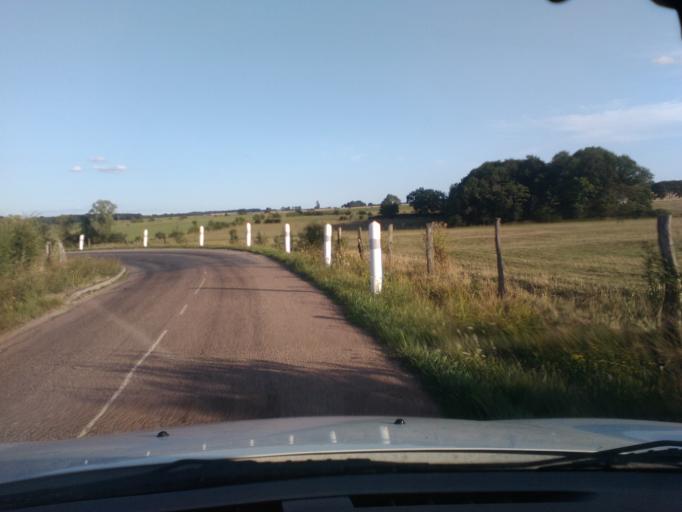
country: FR
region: Lorraine
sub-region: Departement des Vosges
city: Mirecourt
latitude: 48.3502
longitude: 6.0510
